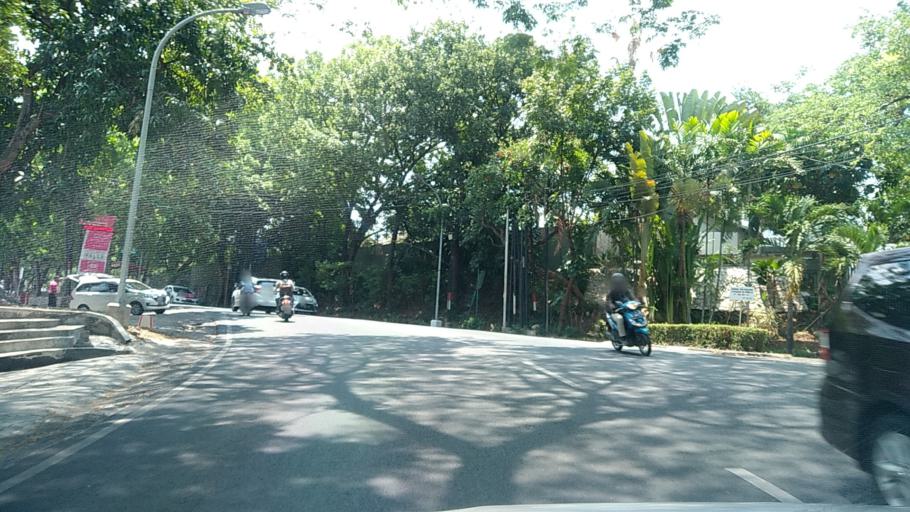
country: ID
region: Central Java
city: Semarang
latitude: -7.0010
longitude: 110.4190
